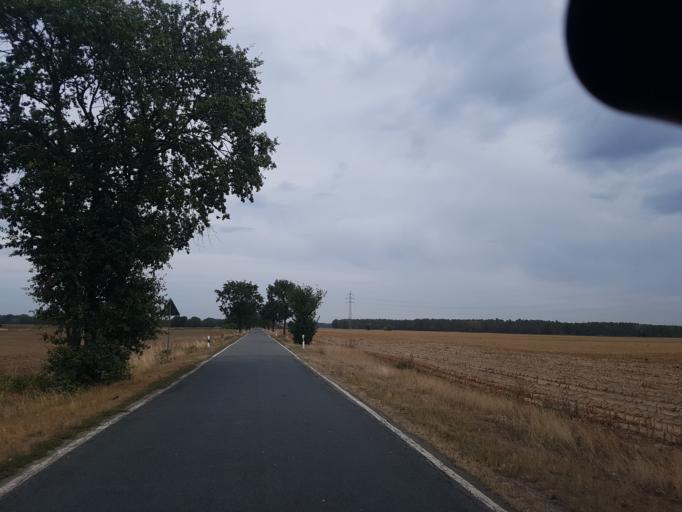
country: DE
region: Saxony-Anhalt
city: Annaburg
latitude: 51.7768
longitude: 13.0559
